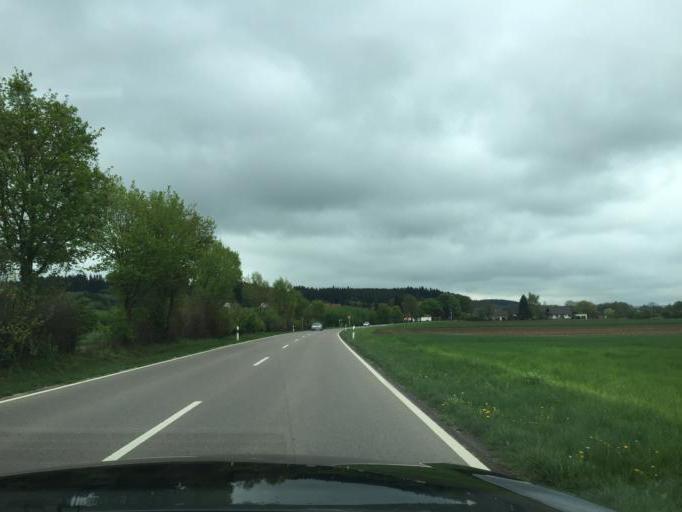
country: DE
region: Bavaria
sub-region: Swabia
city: Buttenwiesen
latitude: 48.5915
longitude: 10.7209
